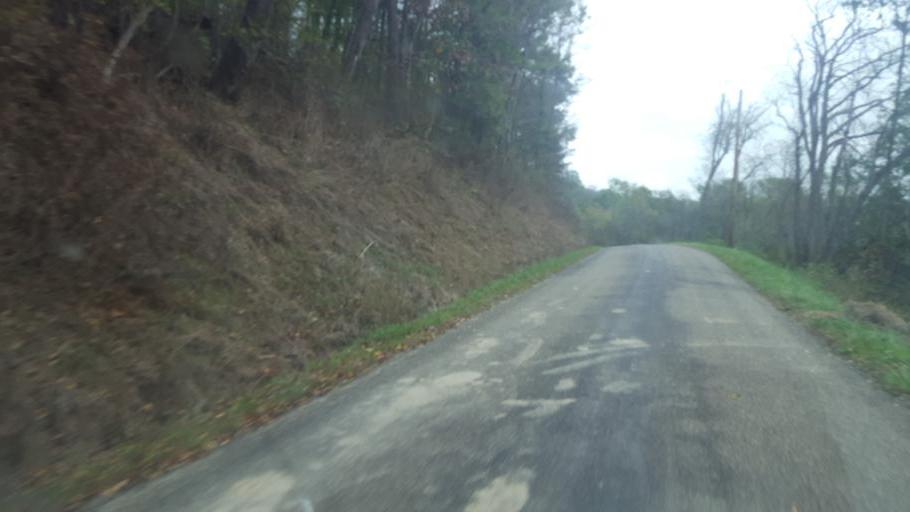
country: US
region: Ohio
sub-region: Carroll County
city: Carrollton
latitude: 40.4318
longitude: -81.0138
